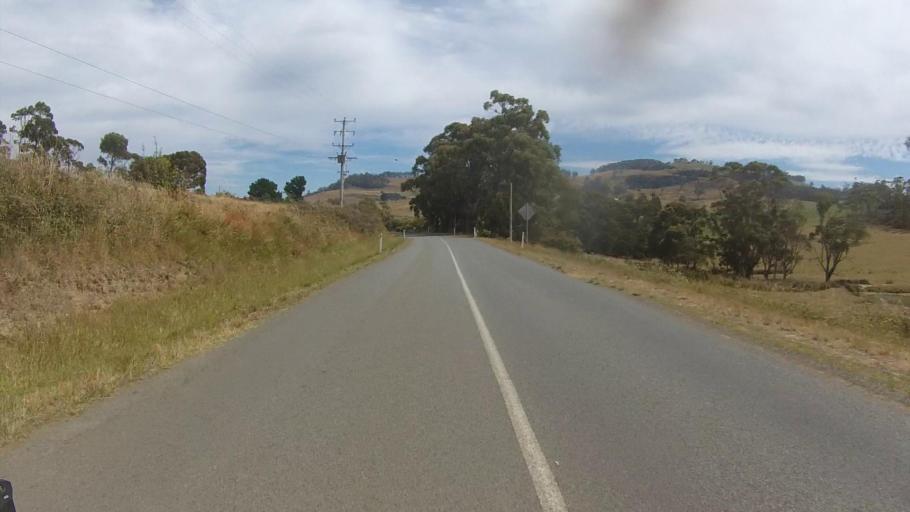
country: AU
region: Tasmania
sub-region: Sorell
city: Sorell
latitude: -42.8217
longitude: 147.8212
